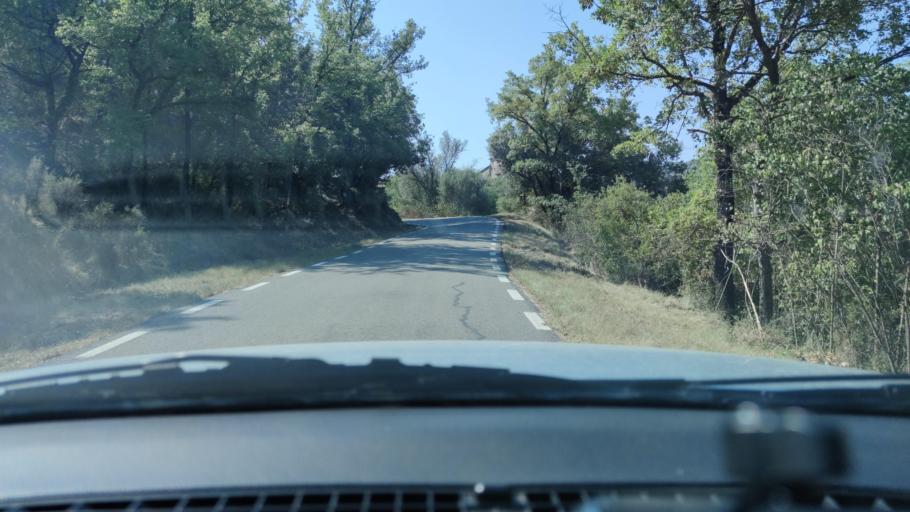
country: ES
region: Catalonia
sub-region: Provincia de Lleida
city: Senterada
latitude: 42.2770
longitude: 0.9430
